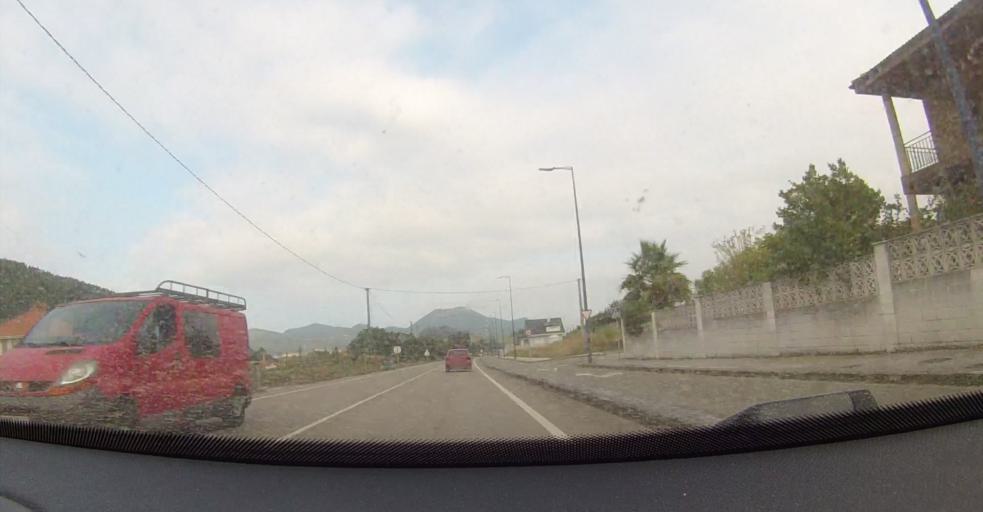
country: ES
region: Cantabria
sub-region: Provincia de Cantabria
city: Argonos
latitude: 43.4577
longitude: -3.5027
